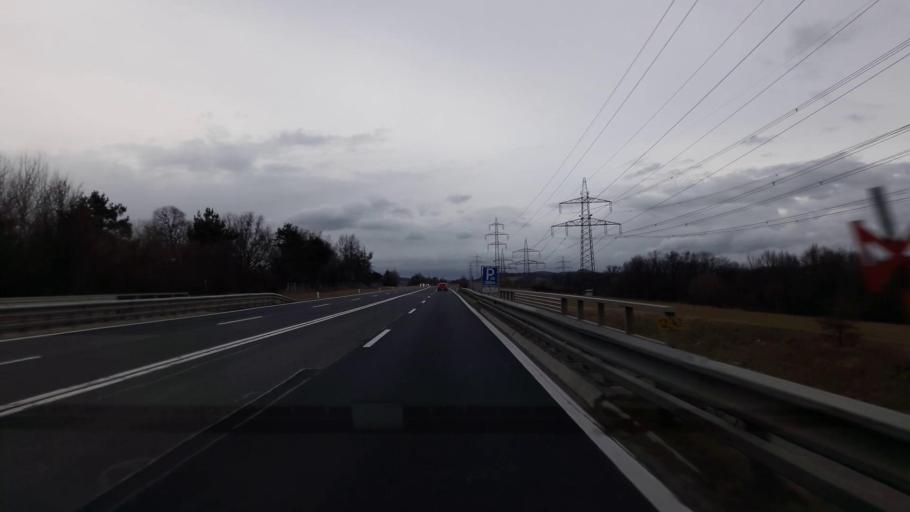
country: AT
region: Burgenland
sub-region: Politischer Bezirk Oberpullendorf
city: Kobersdorf
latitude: 47.6042
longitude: 16.3994
